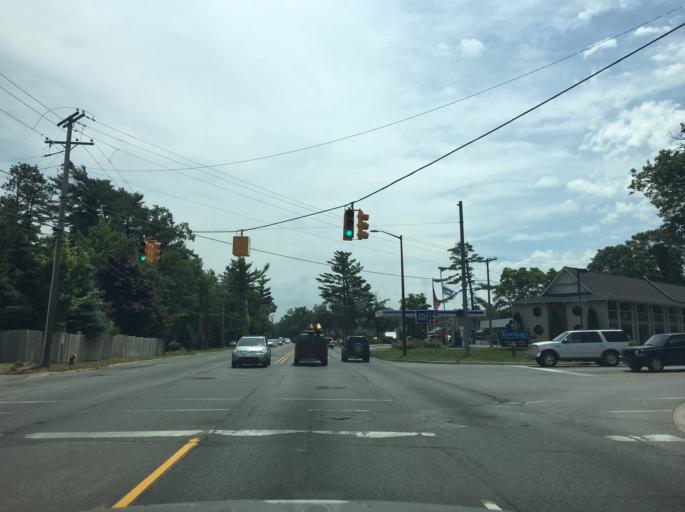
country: US
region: Michigan
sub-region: Grand Traverse County
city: Traverse City
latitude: 44.7566
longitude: -85.5757
